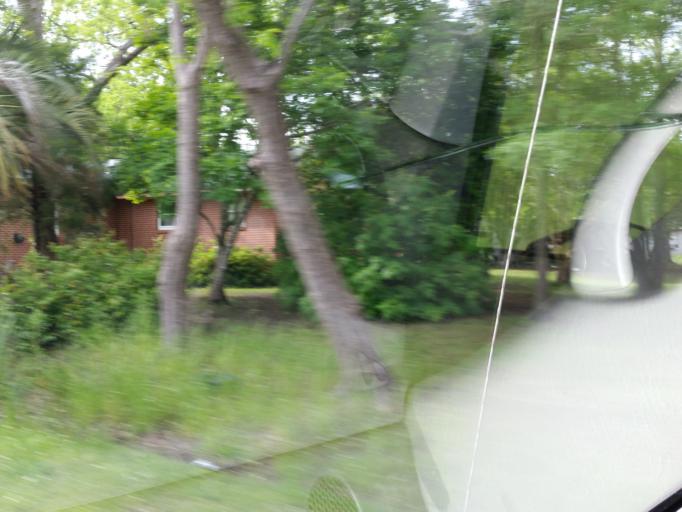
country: US
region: Georgia
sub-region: Dooly County
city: Unadilla
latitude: 32.2595
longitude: -83.7384
